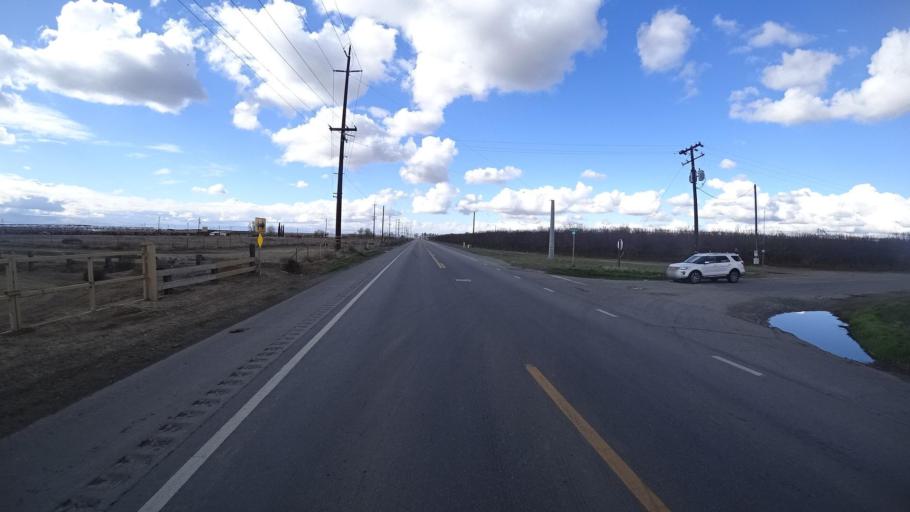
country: US
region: California
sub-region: Kern County
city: Greenfield
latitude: 35.2089
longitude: -119.0922
